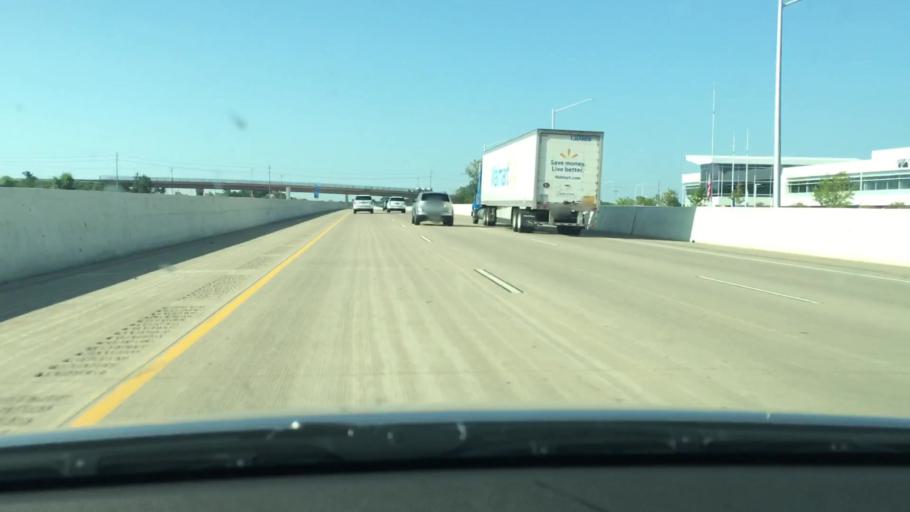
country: US
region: Wisconsin
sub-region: Winnebago County
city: Neenah
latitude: 44.1453
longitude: -88.4893
